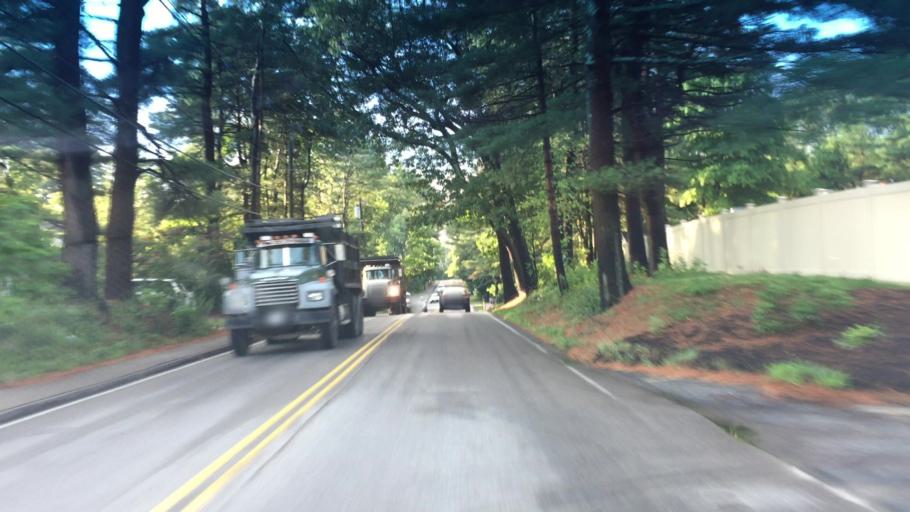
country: US
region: Massachusetts
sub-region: Norfolk County
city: Medfield
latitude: 42.1829
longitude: -71.3062
